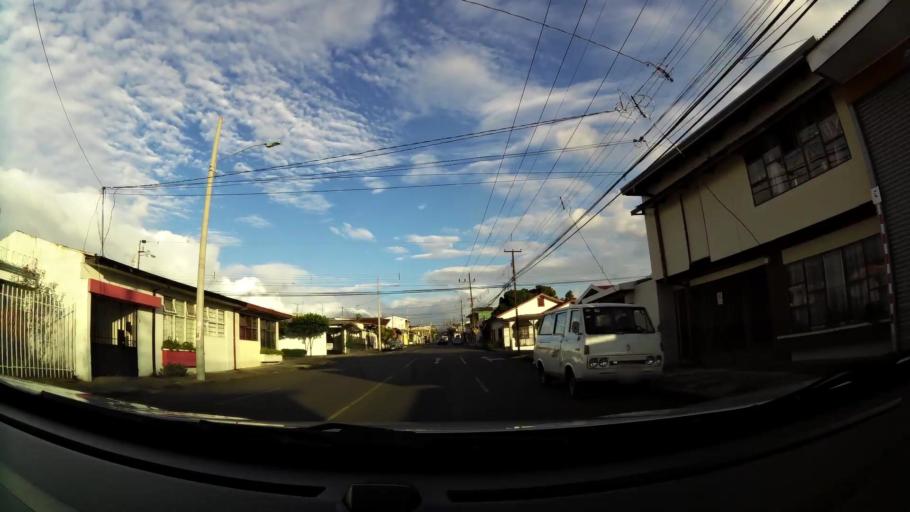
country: CR
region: Heredia
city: Heredia
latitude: 10.0034
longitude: -84.1205
